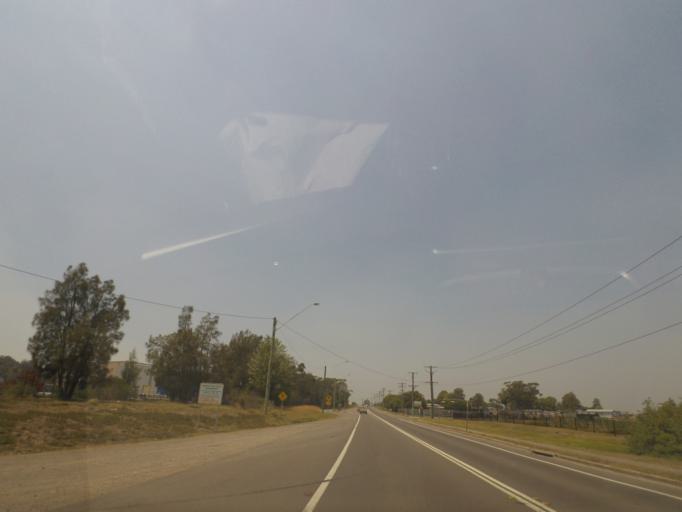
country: AU
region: New South Wales
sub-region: Newcastle
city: Beresfield
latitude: -32.8181
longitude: 151.6976
